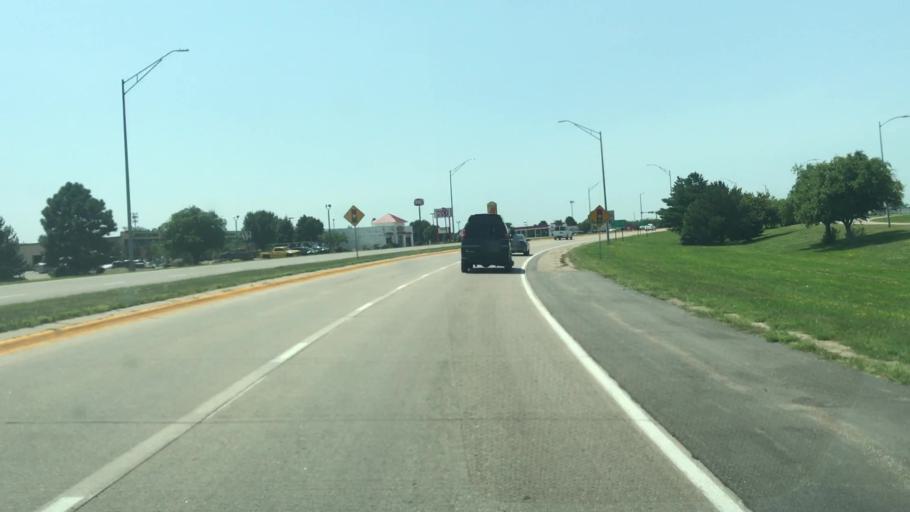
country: US
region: Nebraska
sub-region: Adams County
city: Hastings
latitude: 40.6107
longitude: -98.3840
